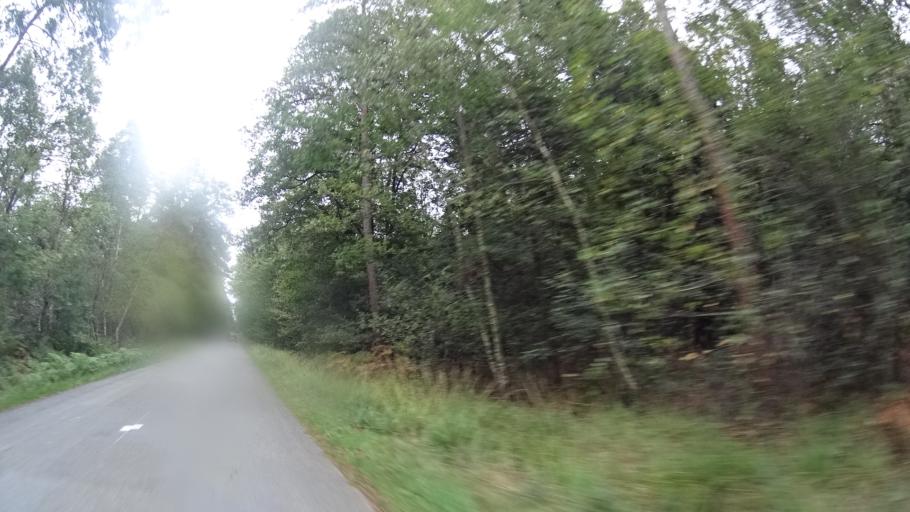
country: FR
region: Brittany
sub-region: Departement d'Ille-et-Vilaine
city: Paimpont
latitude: 48.0759
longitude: -2.1611
